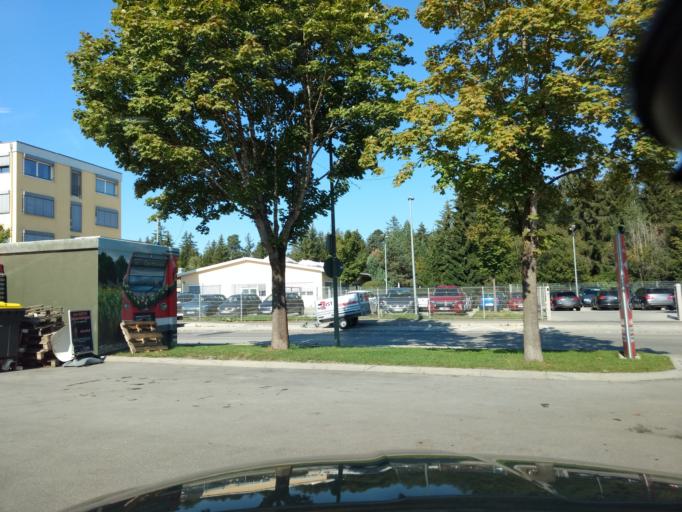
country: DE
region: Bavaria
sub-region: Upper Bavaria
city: Geretsried
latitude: 47.8841
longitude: 11.4610
